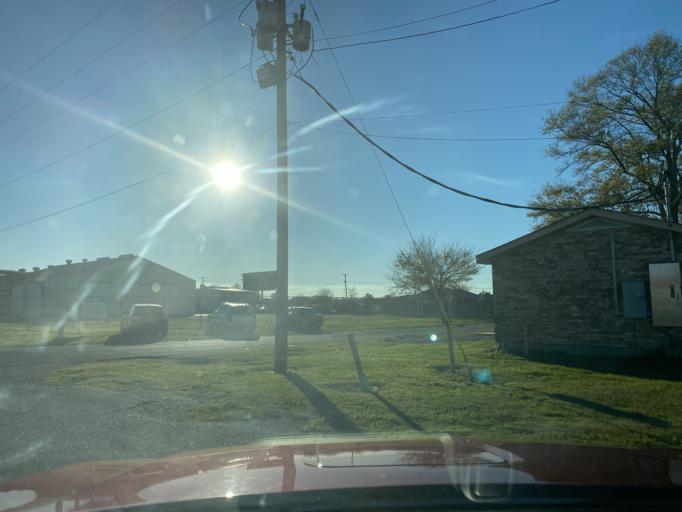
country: US
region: Louisiana
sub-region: Jefferson Parish
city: Kenner
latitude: 29.9829
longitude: -90.2486
